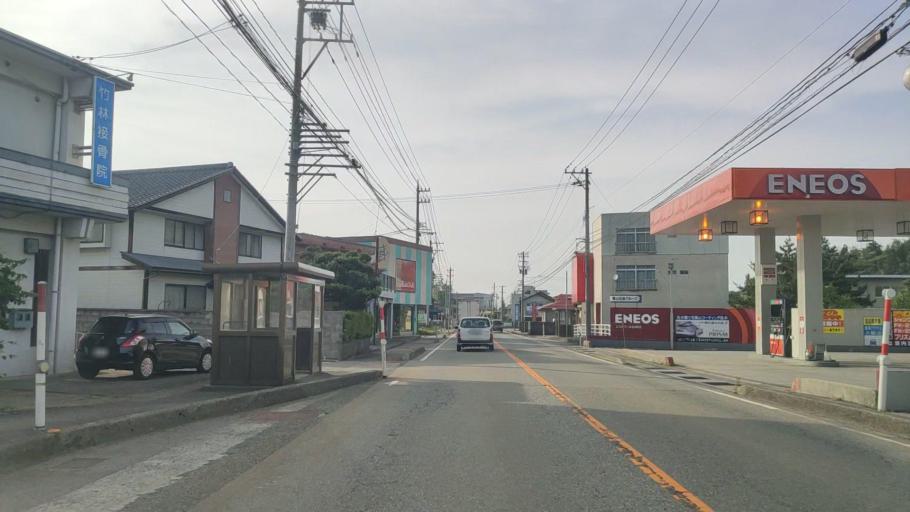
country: JP
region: Toyama
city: Yatsuomachi-higashikumisaka
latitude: 36.5745
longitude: 137.2087
